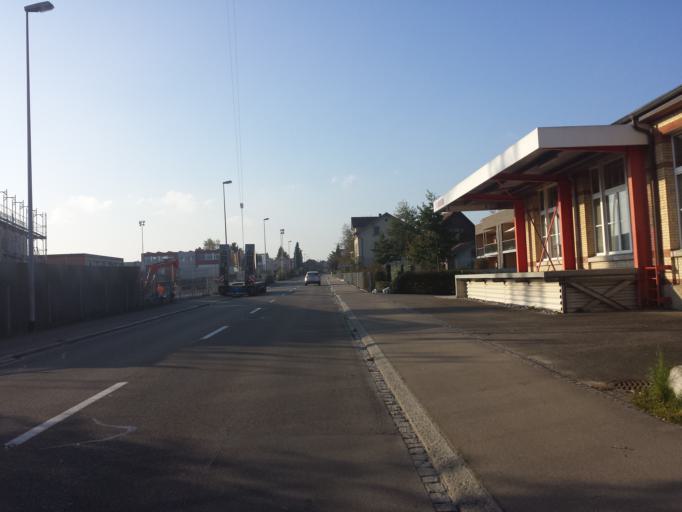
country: CH
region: Thurgau
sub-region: Arbon District
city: Romanshorn
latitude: 47.5704
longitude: 9.3748
